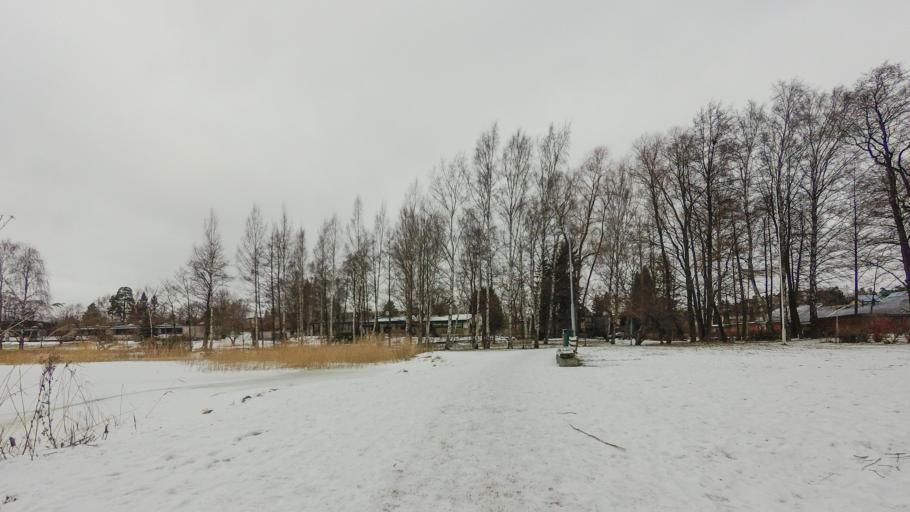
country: FI
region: Uusimaa
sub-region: Helsinki
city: Vantaa
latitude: 60.1890
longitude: 25.0606
